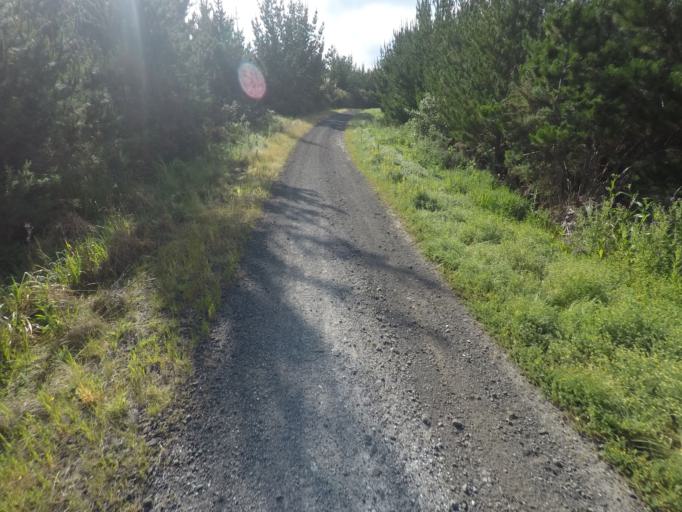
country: NZ
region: Auckland
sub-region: Auckland
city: Rothesay Bay
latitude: -36.7106
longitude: 174.5869
